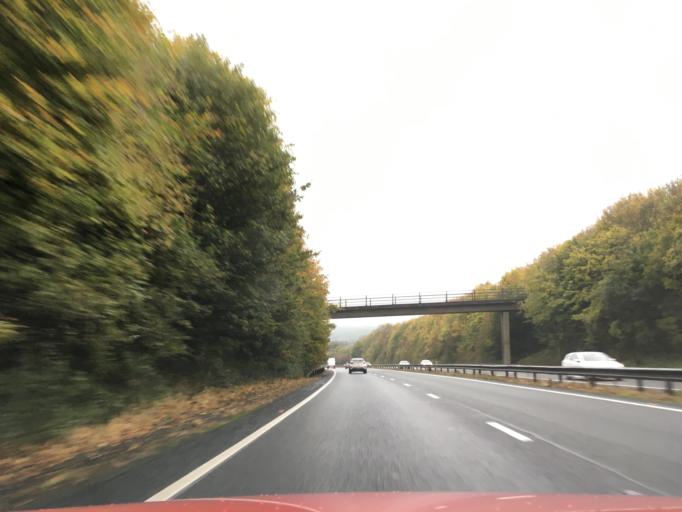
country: GB
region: England
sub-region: Hampshire
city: Highclere
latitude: 51.3297
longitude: -1.3469
